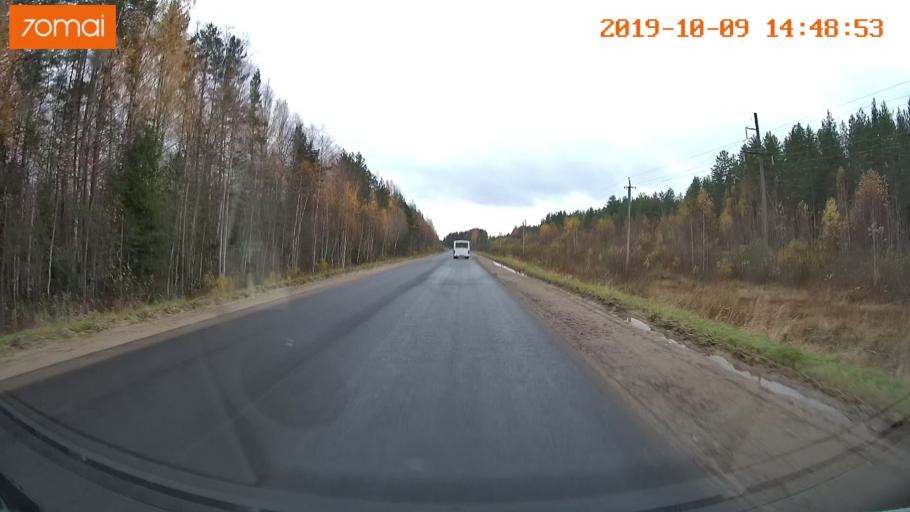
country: RU
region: Kostroma
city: Chistyye Bory
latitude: 58.4001
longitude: 41.5777
